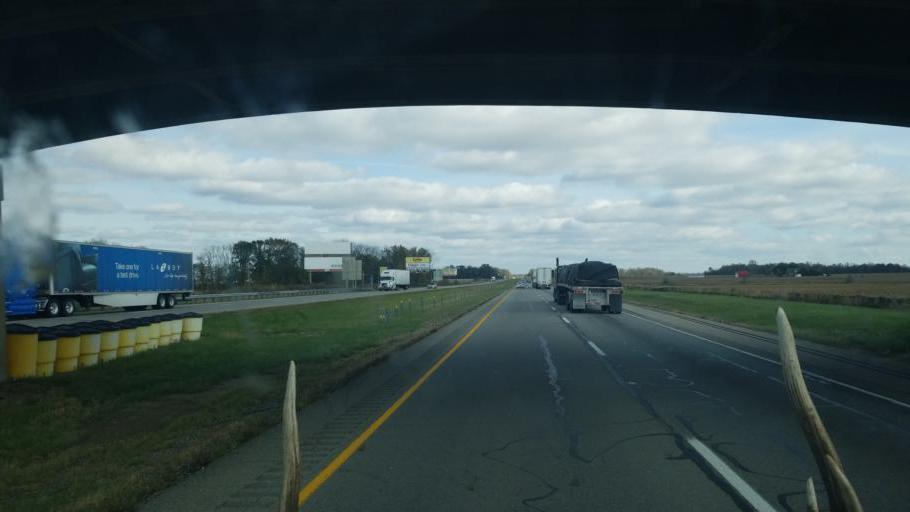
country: US
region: Indiana
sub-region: Henry County
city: New Castle
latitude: 39.8529
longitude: -85.3915
